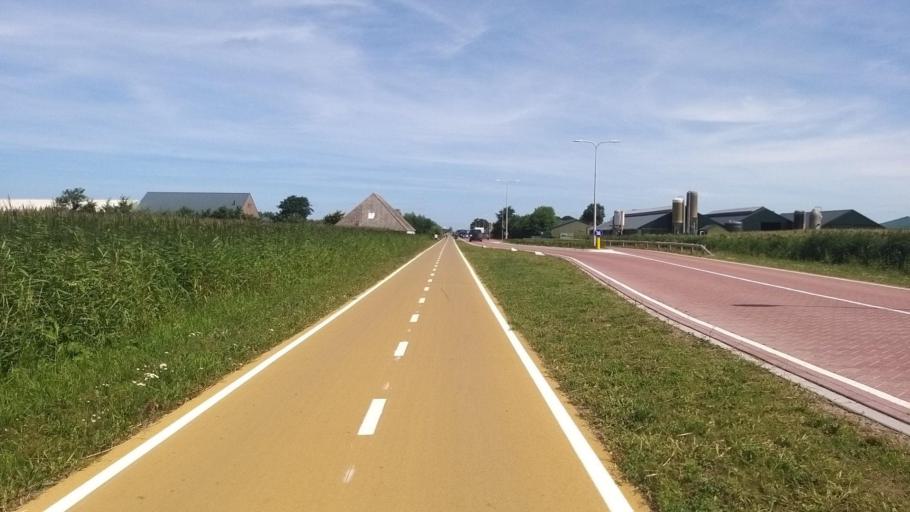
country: NL
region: North Holland
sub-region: Gemeente Texel
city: Den Burg
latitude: 53.1091
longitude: 4.8159
